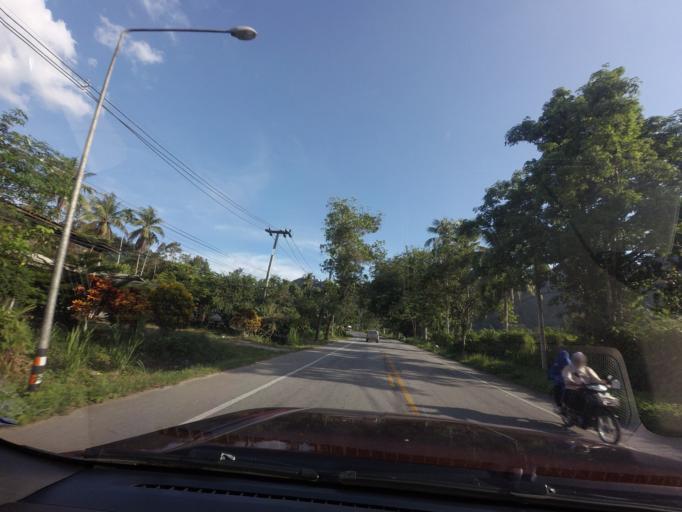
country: TH
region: Yala
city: Than To
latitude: 6.1934
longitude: 101.1732
